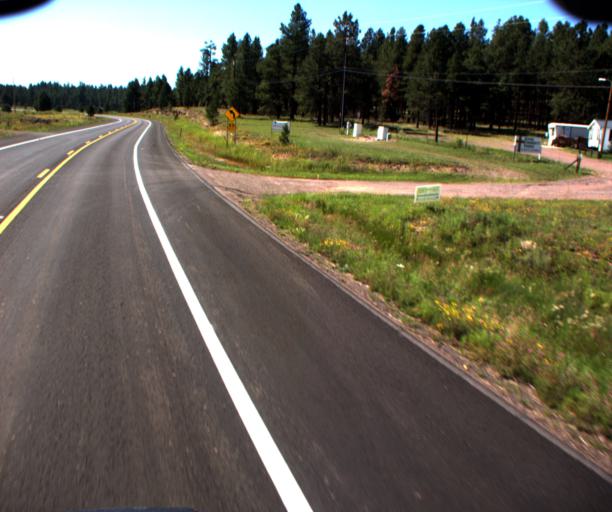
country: US
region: Arizona
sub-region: Apache County
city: Eagar
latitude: 33.8311
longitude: -109.1159
